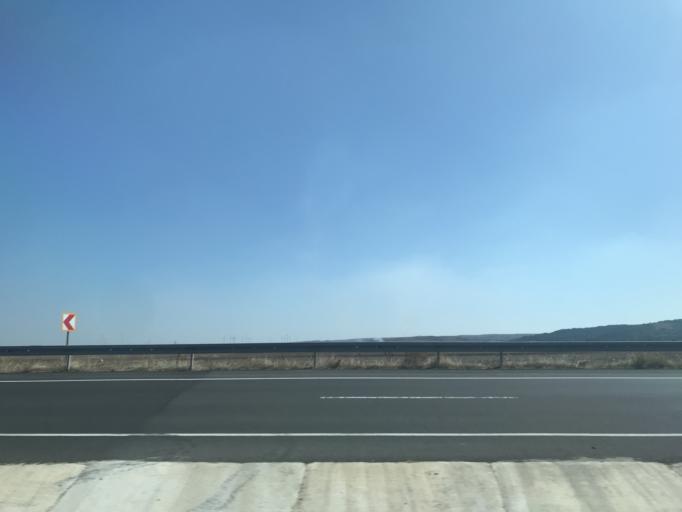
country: TR
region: Tekirdag
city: Muratli
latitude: 41.1649
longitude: 27.5314
